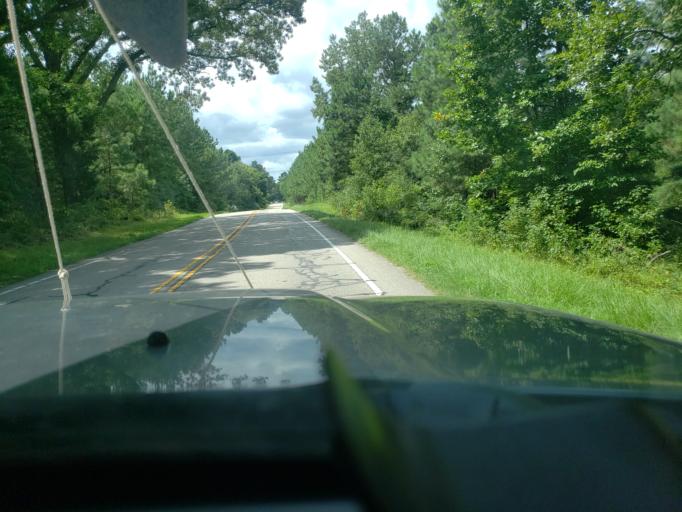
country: US
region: North Carolina
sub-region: Wake County
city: Rolesville
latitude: 35.8782
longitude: -78.4649
